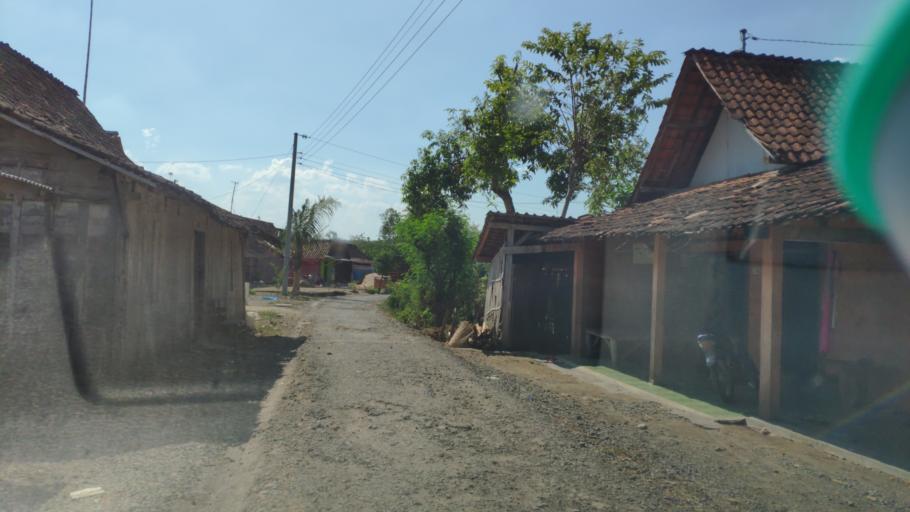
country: ID
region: Central Java
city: Botoh
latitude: -7.0876
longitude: 111.4672
